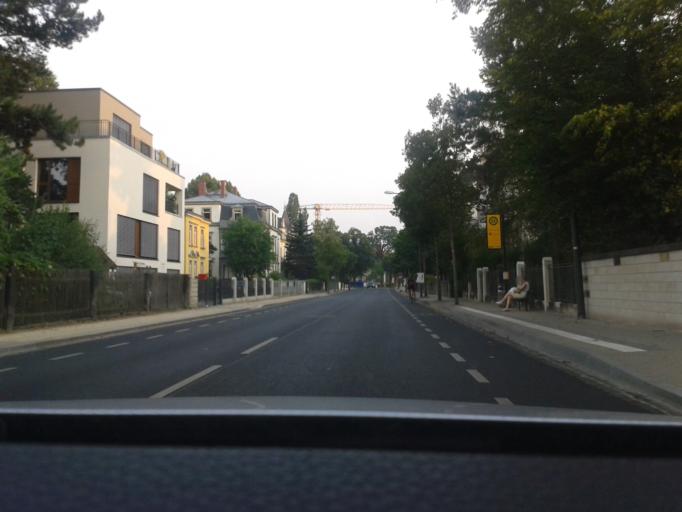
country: DE
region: Saxony
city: Albertstadt
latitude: 51.0469
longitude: 13.8089
